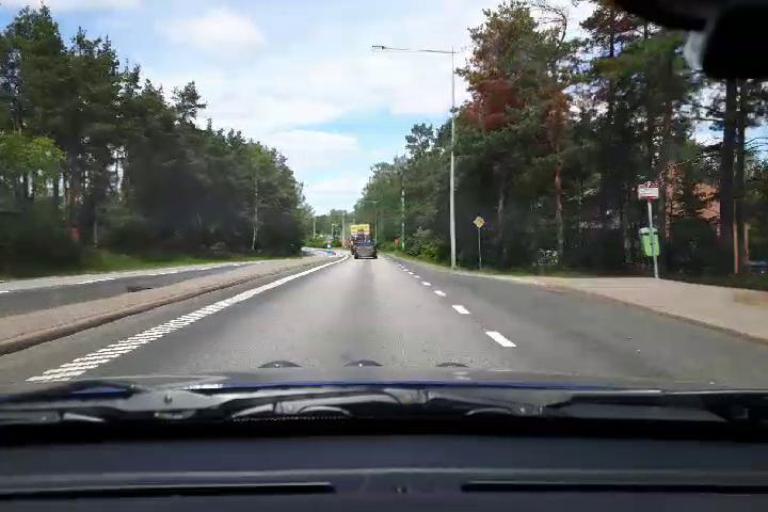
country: SE
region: Uppsala
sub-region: Osthammars Kommun
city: Bjorklinge
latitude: 60.0325
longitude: 17.5522
